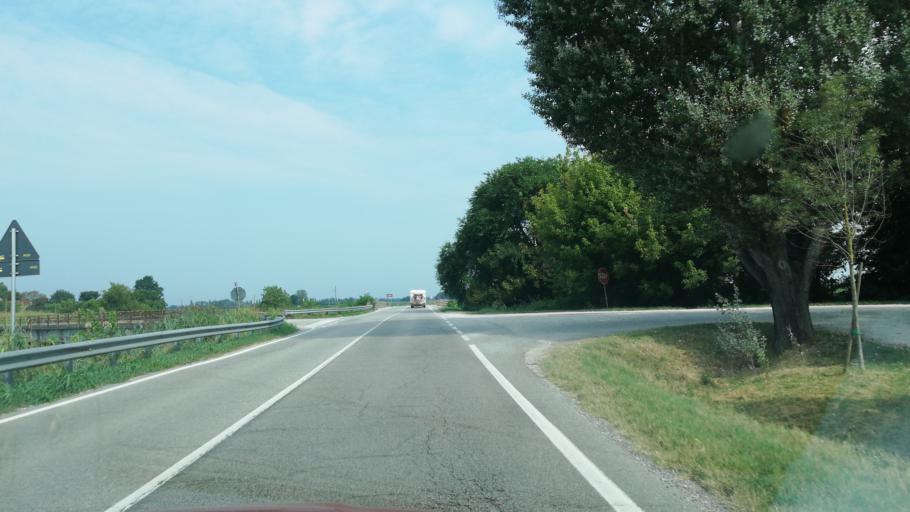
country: IT
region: Veneto
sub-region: Provincia di Venezia
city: La Salute di Livenza
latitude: 45.5999
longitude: 12.8050
